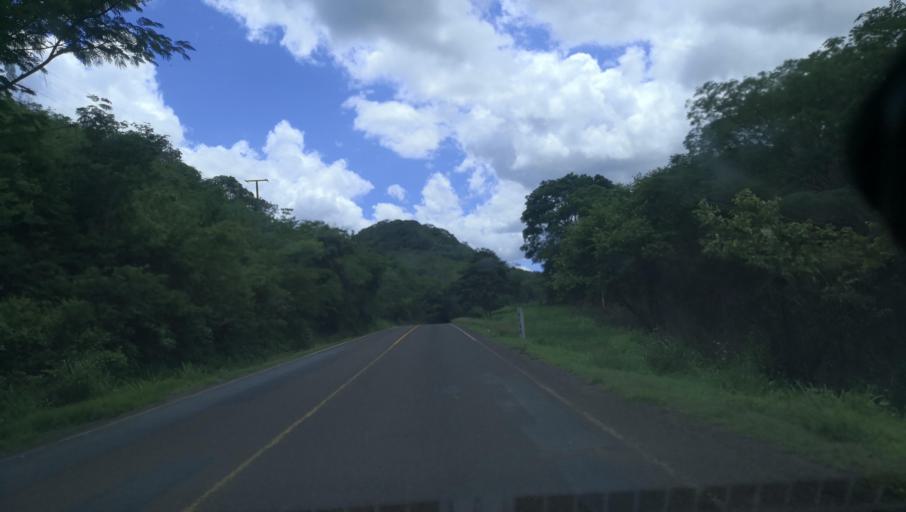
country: NI
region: Madriz
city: Palacaguina
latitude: 13.4362
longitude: -86.4323
